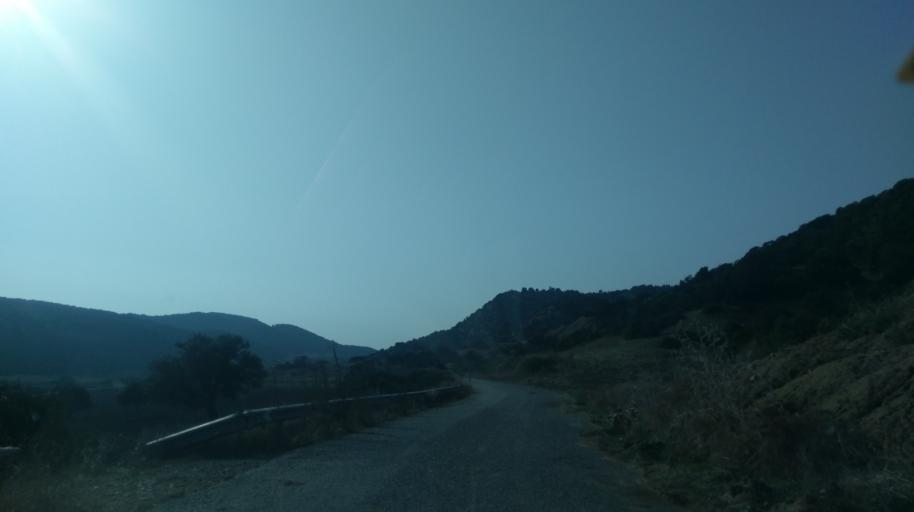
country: CY
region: Ammochostos
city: Rizokarpaso
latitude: 35.5556
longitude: 34.3703
